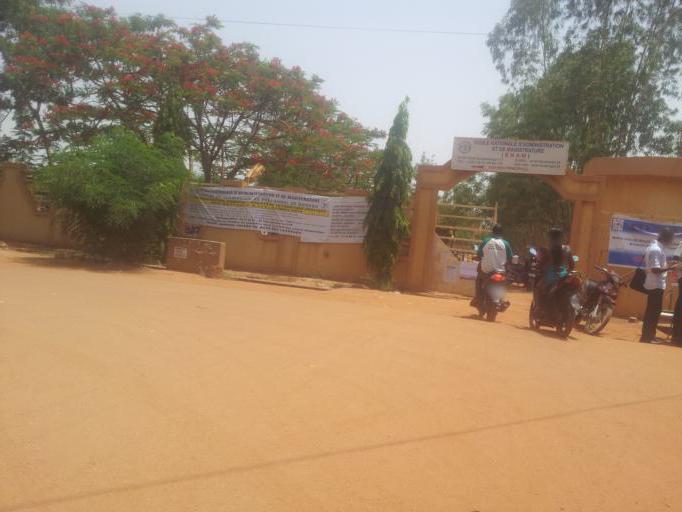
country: BF
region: Centre
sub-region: Kadiogo Province
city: Ouagadougou
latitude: 12.3775
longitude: -1.5049
